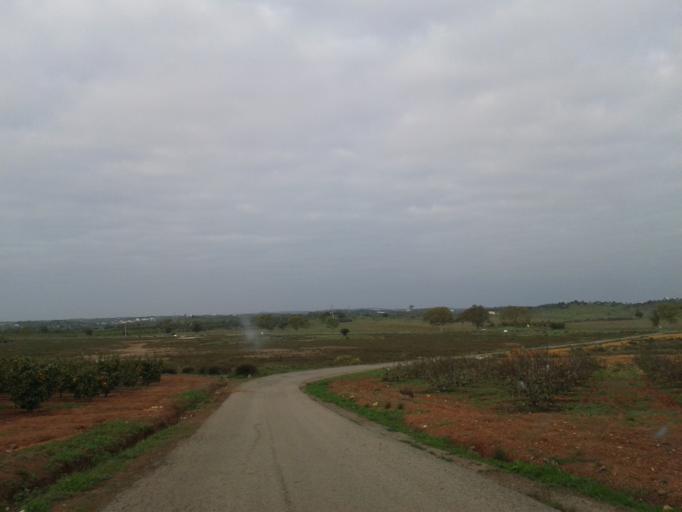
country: PT
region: Faro
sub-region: Vila Real de Santo Antonio
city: Monte Gordo
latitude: 37.2002
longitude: -7.4750
